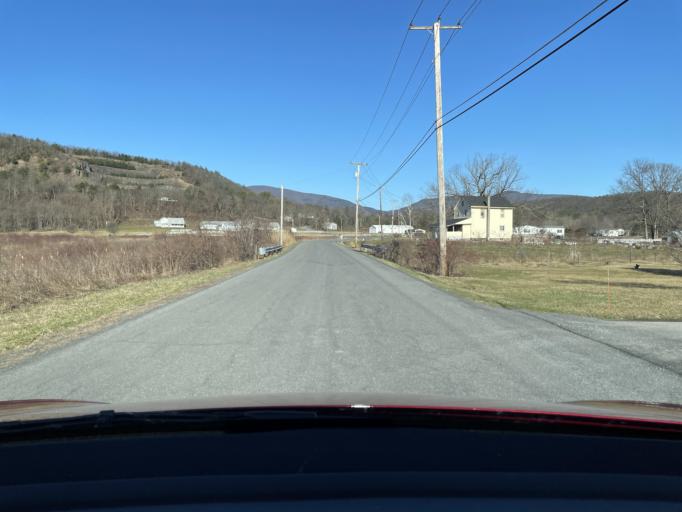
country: US
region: New York
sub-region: Ulster County
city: Saugerties
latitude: 42.0741
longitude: -73.9815
